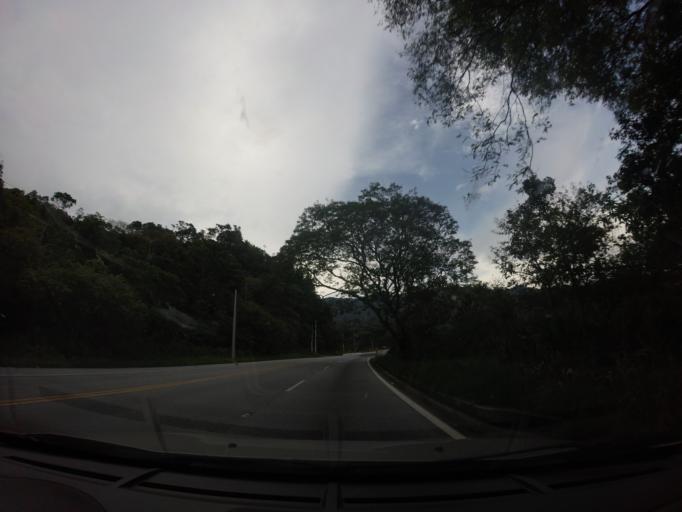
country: BR
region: Sao Paulo
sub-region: Campos Do Jordao
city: Campos do Jordao
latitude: -22.8256
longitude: -45.6267
